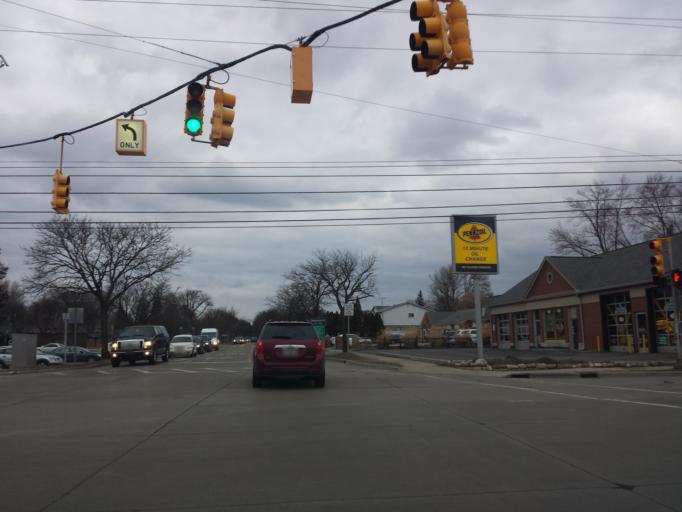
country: US
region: Michigan
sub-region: Oakland County
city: Beverly Hills
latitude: 42.5313
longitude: -83.2239
